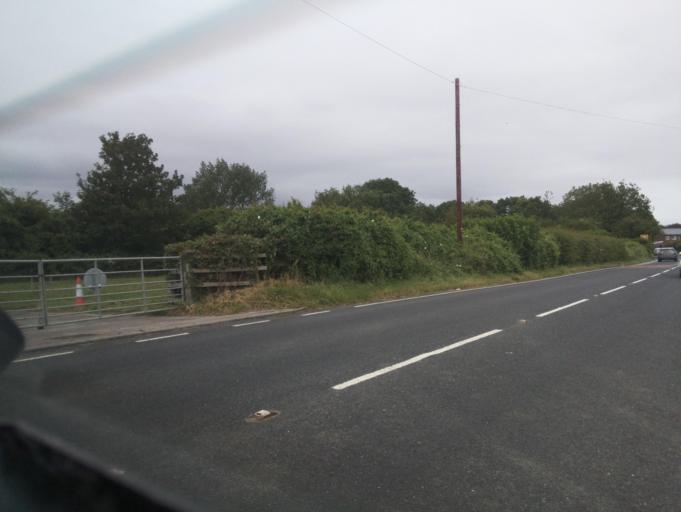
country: GB
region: Wales
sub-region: Vale of Glamorgan
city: Penarth
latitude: 51.4143
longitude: -3.1822
